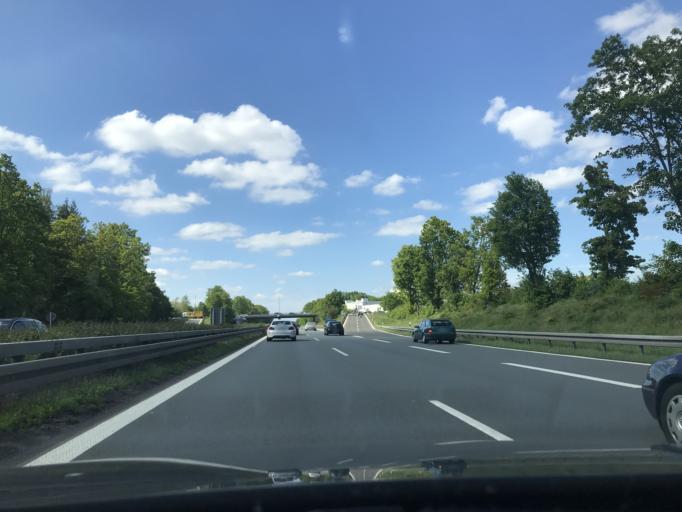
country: DE
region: Bavaria
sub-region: Regierungsbezirk Mittelfranken
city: Furth
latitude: 49.4928
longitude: 11.0007
